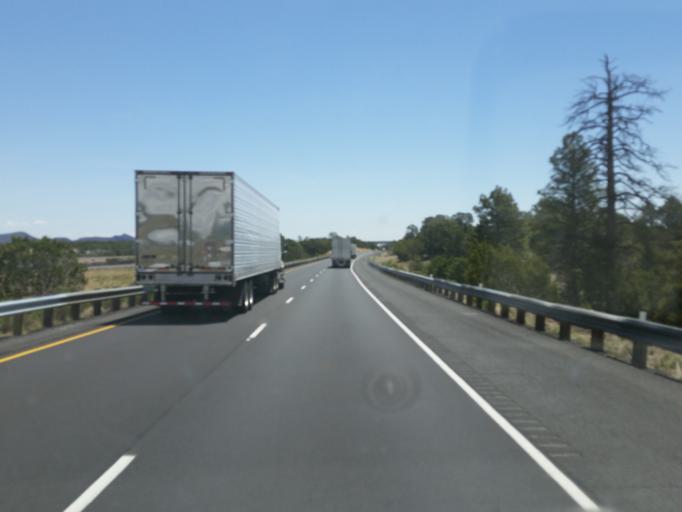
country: US
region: Arizona
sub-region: Coconino County
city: Flagstaff
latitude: 35.2061
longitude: -111.5034
